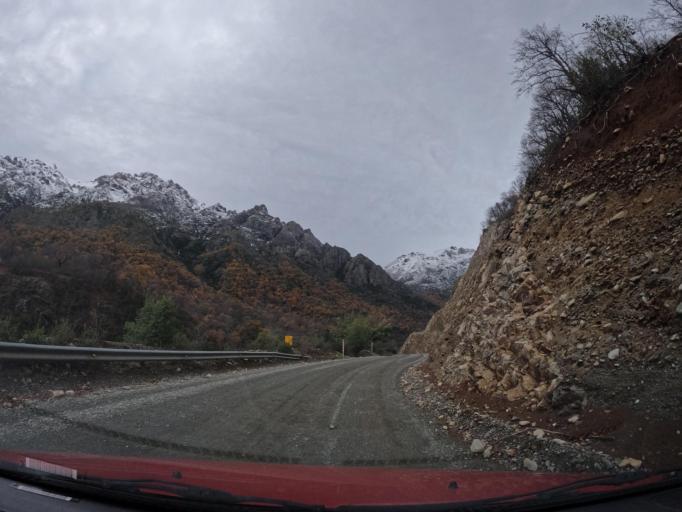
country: CL
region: Maule
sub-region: Provincia de Linares
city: Colbun
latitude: -35.8608
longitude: -71.1285
